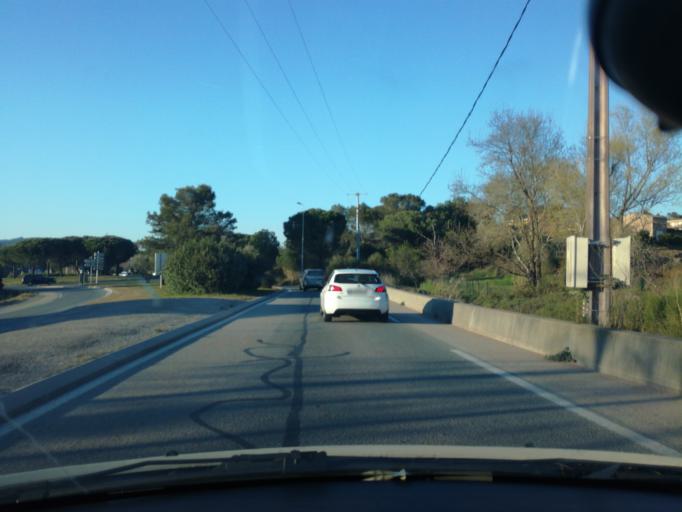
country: FR
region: Provence-Alpes-Cote d'Azur
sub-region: Departement du Var
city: Frejus
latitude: 43.4700
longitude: 6.7447
